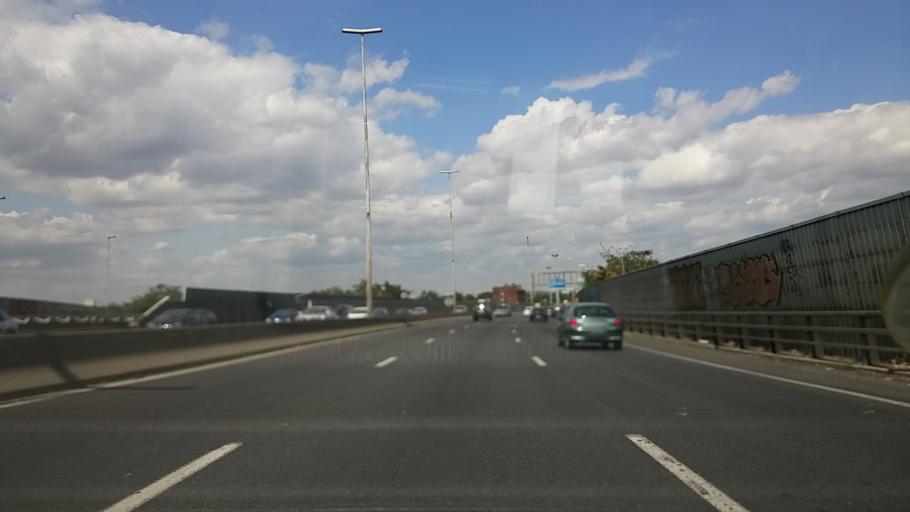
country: FR
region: Ile-de-France
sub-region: Departement de Seine-Saint-Denis
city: Noisy-le-Sec
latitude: 48.8999
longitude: 2.4696
